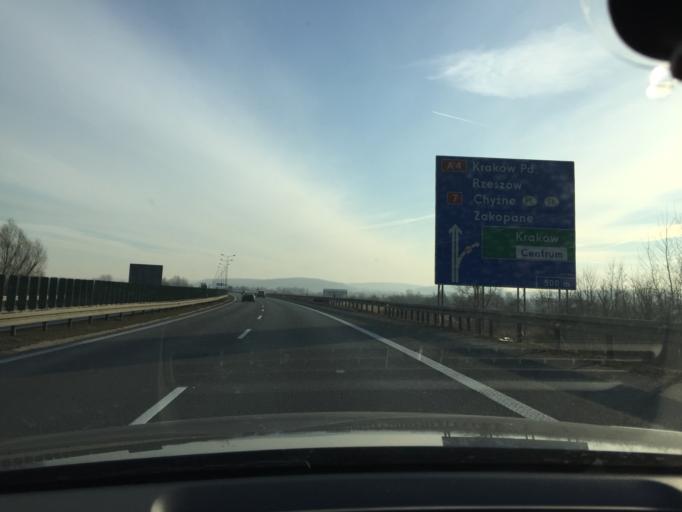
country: PL
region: Lesser Poland Voivodeship
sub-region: Powiat krakowski
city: Kryspinow
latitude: 50.0422
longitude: 19.8077
